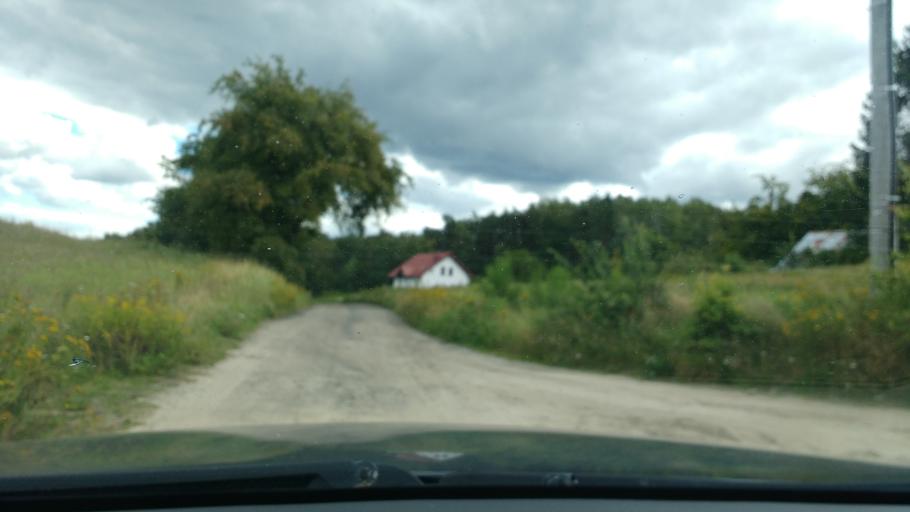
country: PL
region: Pomeranian Voivodeship
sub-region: Powiat kartuski
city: Chwaszczyno
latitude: 54.4749
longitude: 18.4318
